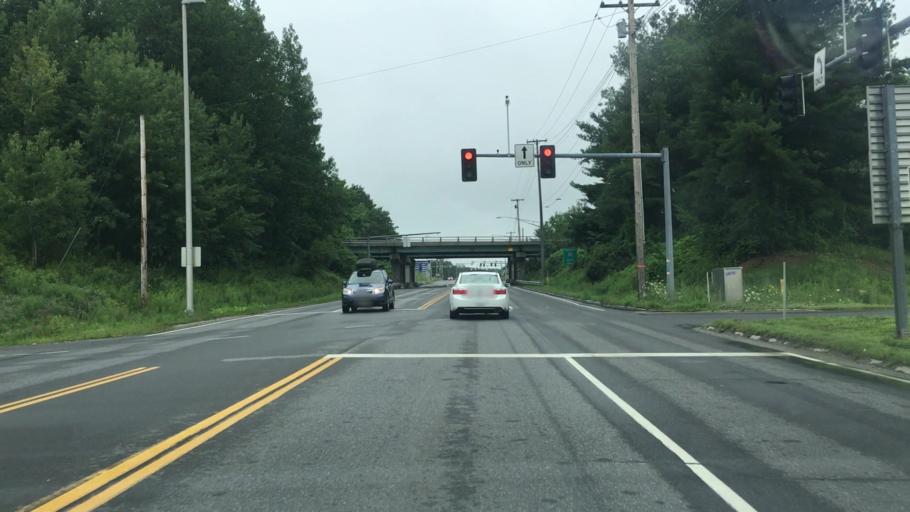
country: US
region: Maine
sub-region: Kennebec County
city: Augusta
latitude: 44.3472
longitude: -69.7952
